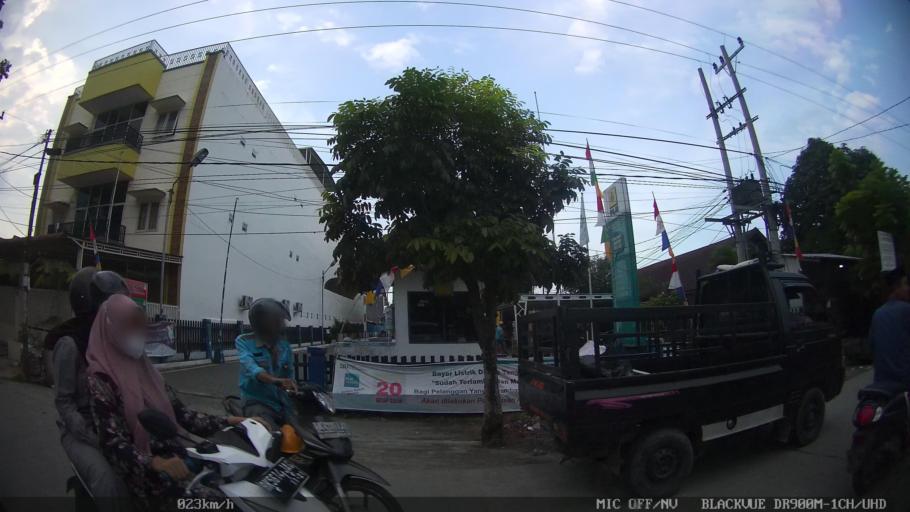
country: ID
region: North Sumatra
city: Medan
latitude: 3.6094
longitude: 98.7020
